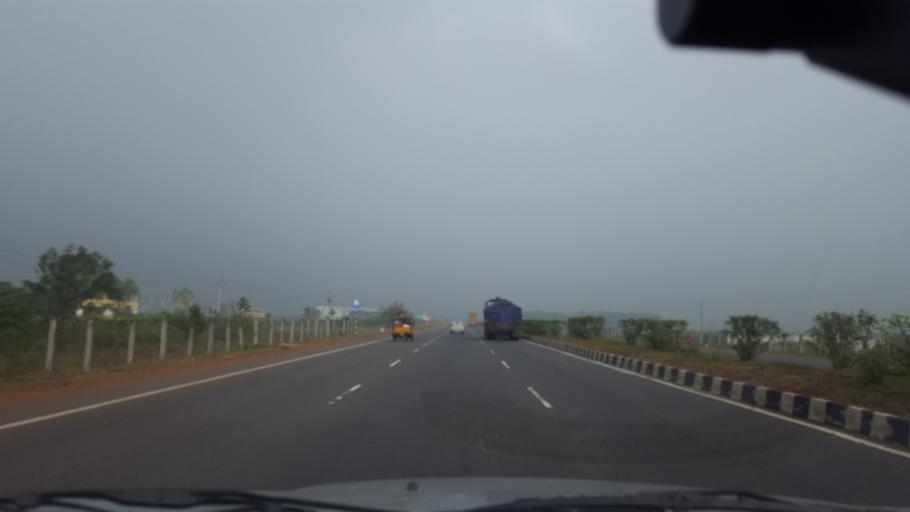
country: IN
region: Andhra Pradesh
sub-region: Prakasam
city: Ongole
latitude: 15.5741
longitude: 80.0439
